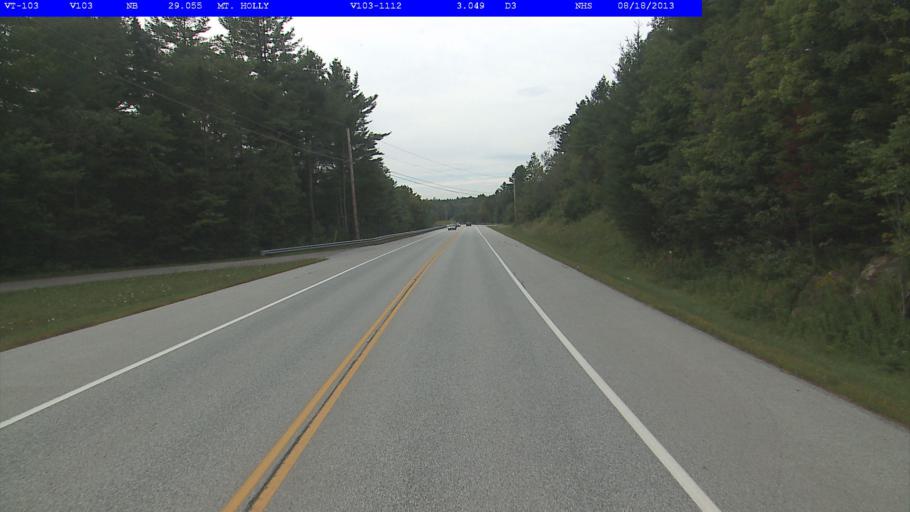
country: US
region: Vermont
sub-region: Rutland County
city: Rutland
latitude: 43.4520
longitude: -72.7866
